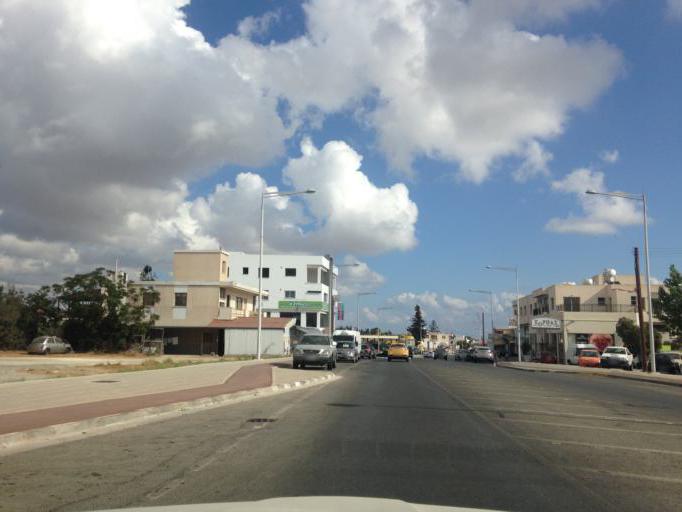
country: CY
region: Pafos
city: Paphos
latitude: 34.7642
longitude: 32.4475
